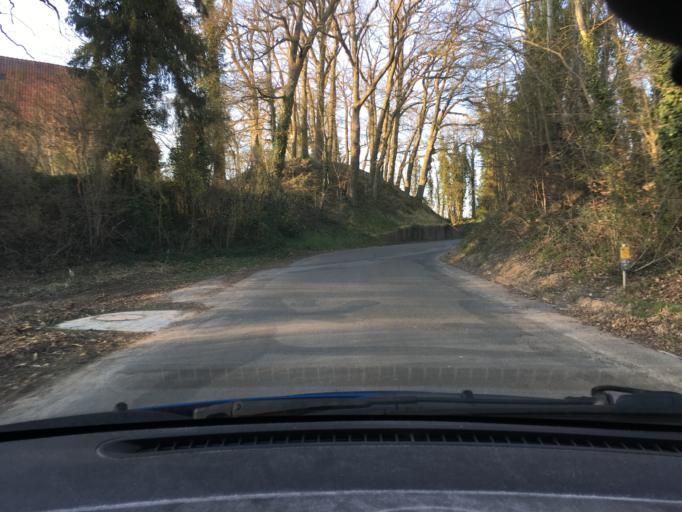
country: DE
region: Lower Saxony
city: Thomasburg
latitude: 53.2306
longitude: 10.6585
